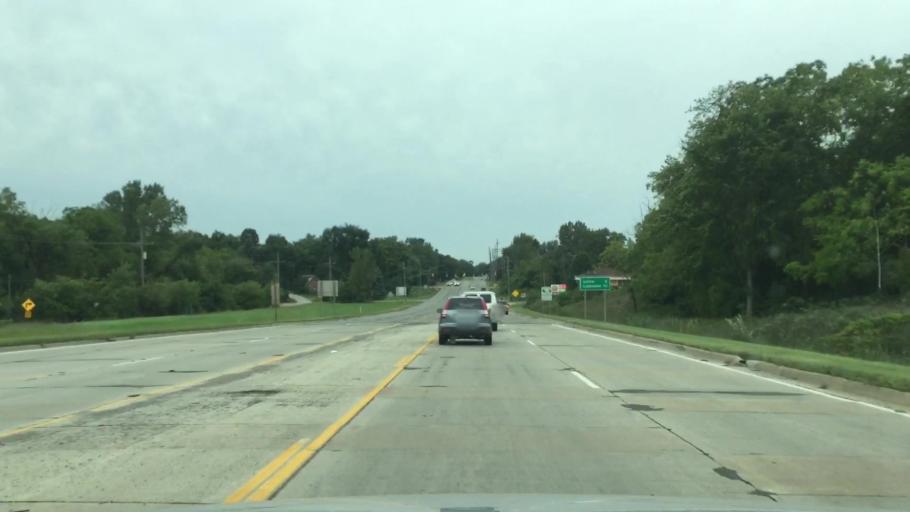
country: US
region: Michigan
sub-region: Washtenaw County
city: Ypsilanti
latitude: 42.2218
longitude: -83.6563
